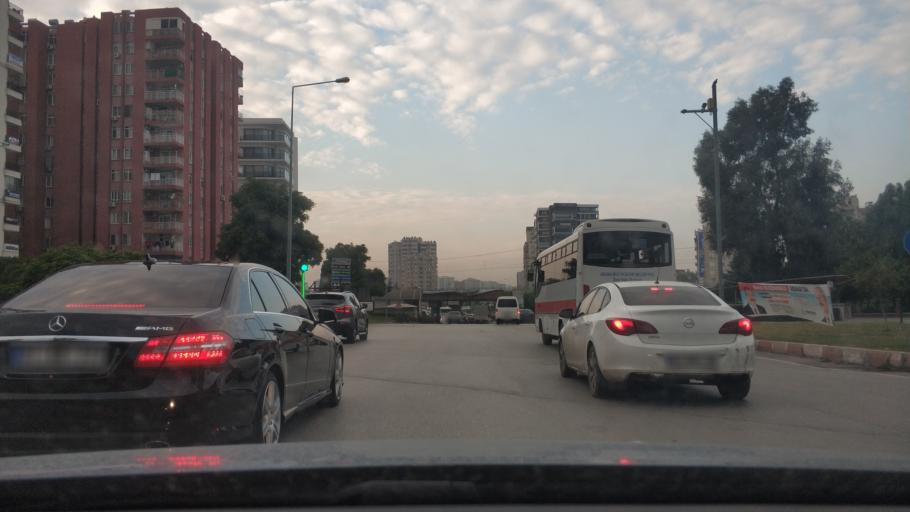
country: TR
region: Adana
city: Adana
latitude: 37.0017
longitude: 35.3139
